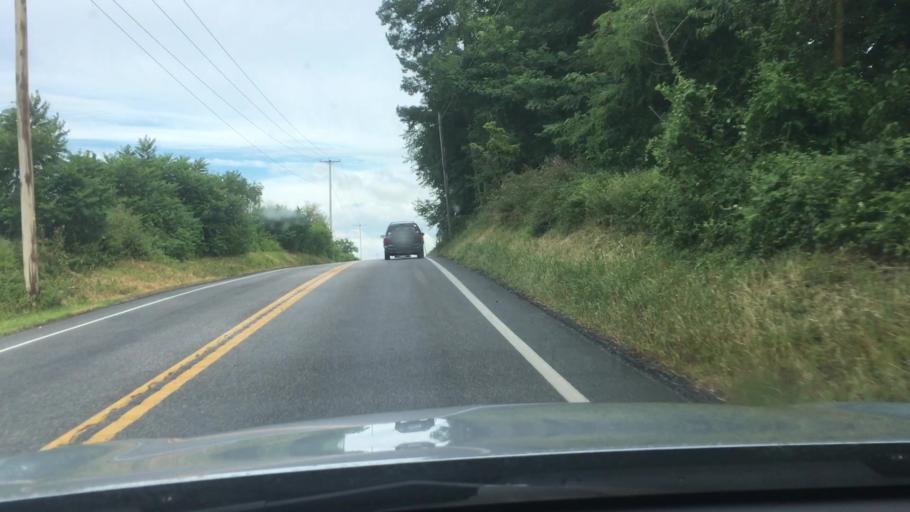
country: US
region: Pennsylvania
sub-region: Cumberland County
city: Boiling Springs
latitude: 40.1659
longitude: -77.1061
